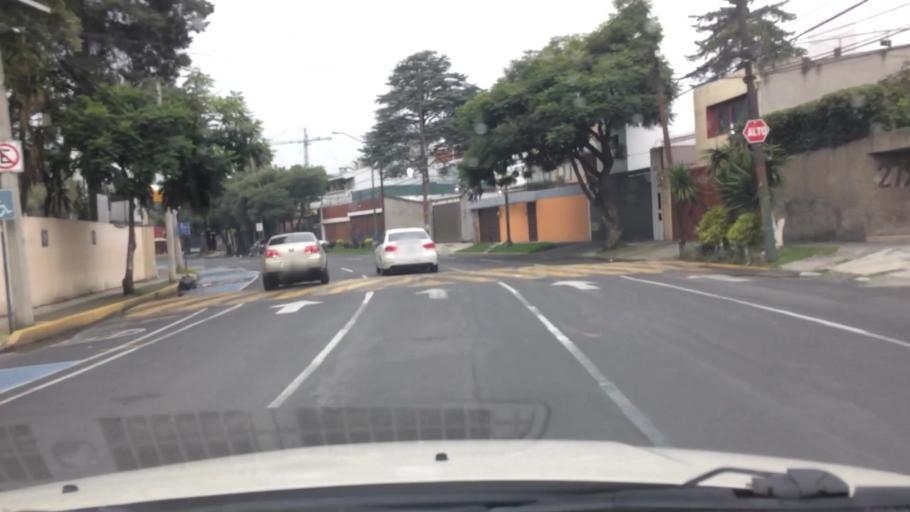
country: MX
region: Mexico City
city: Magdalena Contreras
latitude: 19.3435
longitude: -99.2039
